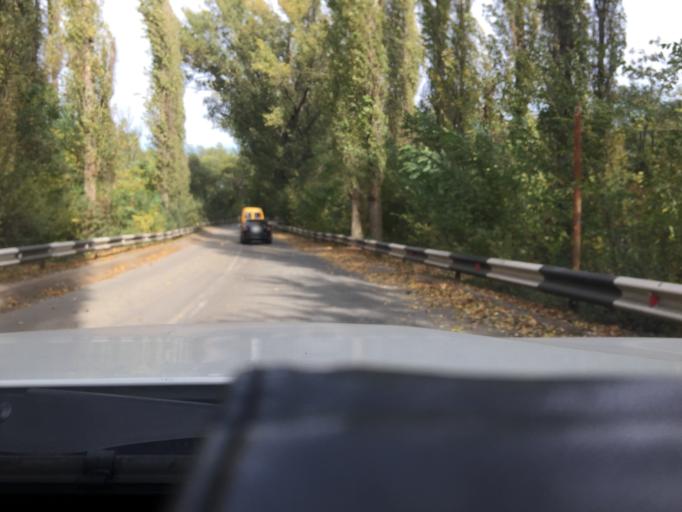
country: RU
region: Rostov
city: Aksay
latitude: 47.3022
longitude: 39.8256
